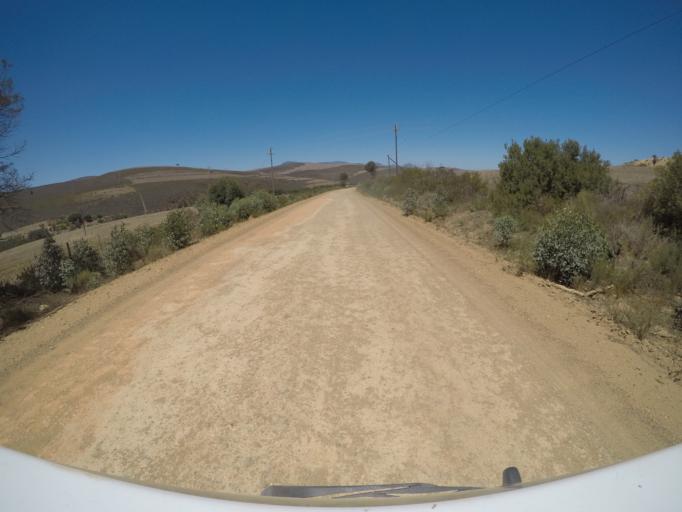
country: ZA
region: Western Cape
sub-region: Overberg District Municipality
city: Caledon
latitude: -34.1898
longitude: 19.2248
